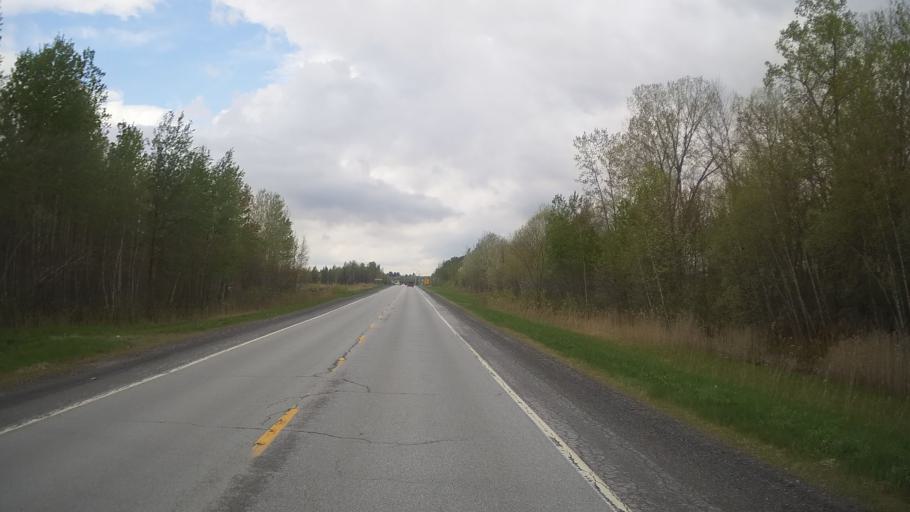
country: CA
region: Quebec
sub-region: Monteregie
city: Farnham
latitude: 45.2727
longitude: -72.9745
